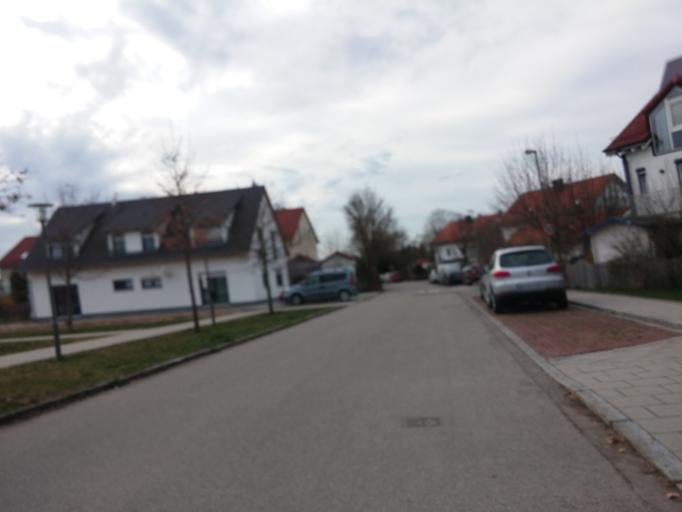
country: DE
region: Bavaria
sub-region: Upper Bavaria
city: Grasbrunn
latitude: 48.0762
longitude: 11.7498
